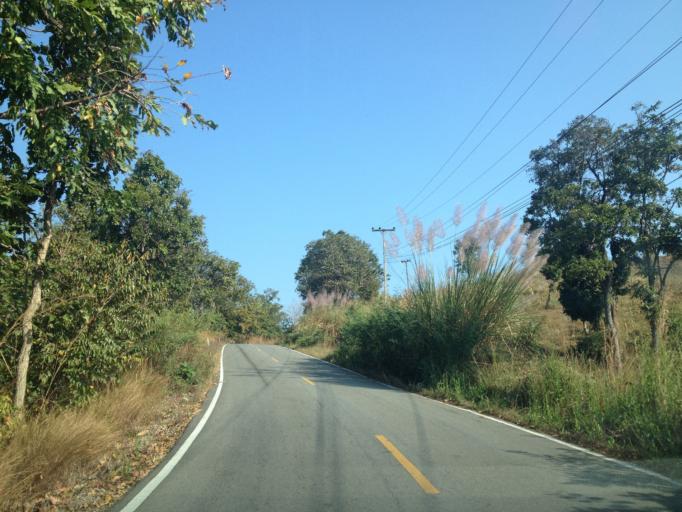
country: TH
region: Mae Hong Son
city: Ban Huai I Huak
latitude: 18.1328
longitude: 98.2217
